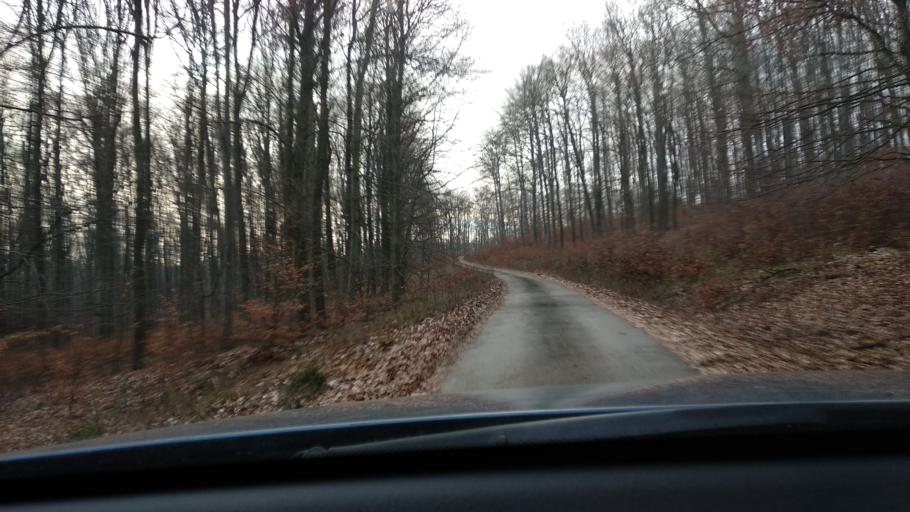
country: SK
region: Trenciansky
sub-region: Okres Trencin
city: Trencin
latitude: 48.8014
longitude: 18.0826
